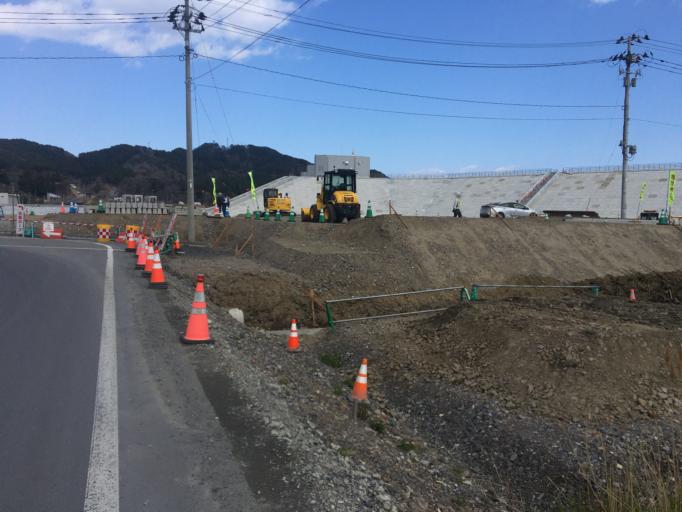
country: JP
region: Iwate
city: Otsuchi
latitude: 39.3573
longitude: 141.9074
